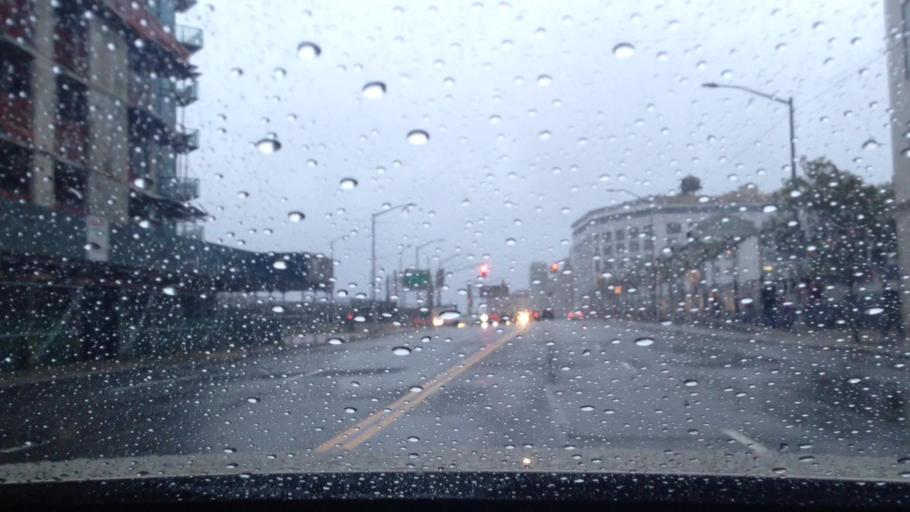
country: US
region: New York
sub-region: Queens County
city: Long Island City
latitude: 40.7461
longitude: -73.9413
